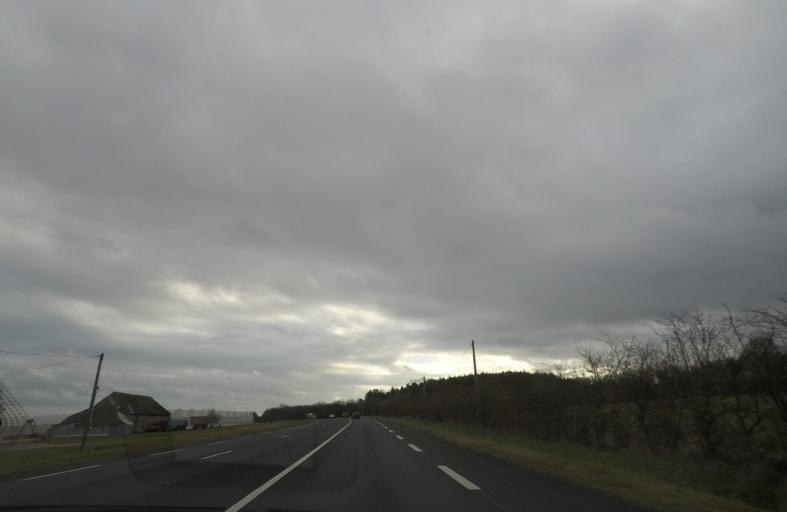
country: FR
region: Centre
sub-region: Departement du Loir-et-Cher
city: Soings-en-Sologne
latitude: 47.4416
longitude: 1.5458
